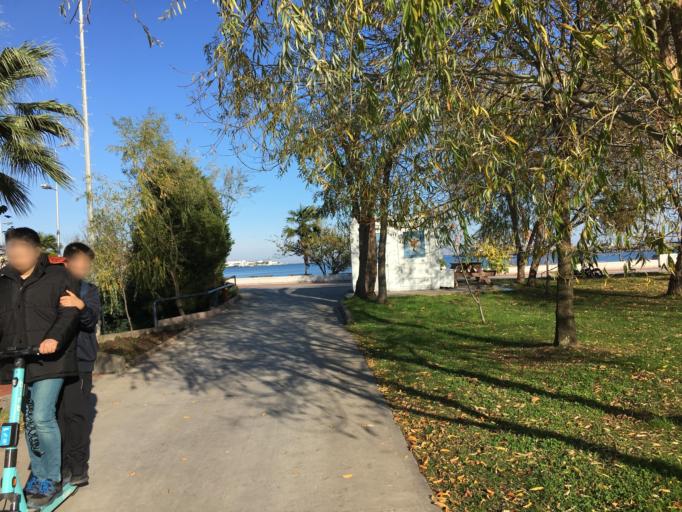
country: TR
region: Samsun
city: Samsun
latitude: 41.2863
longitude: 36.3454
